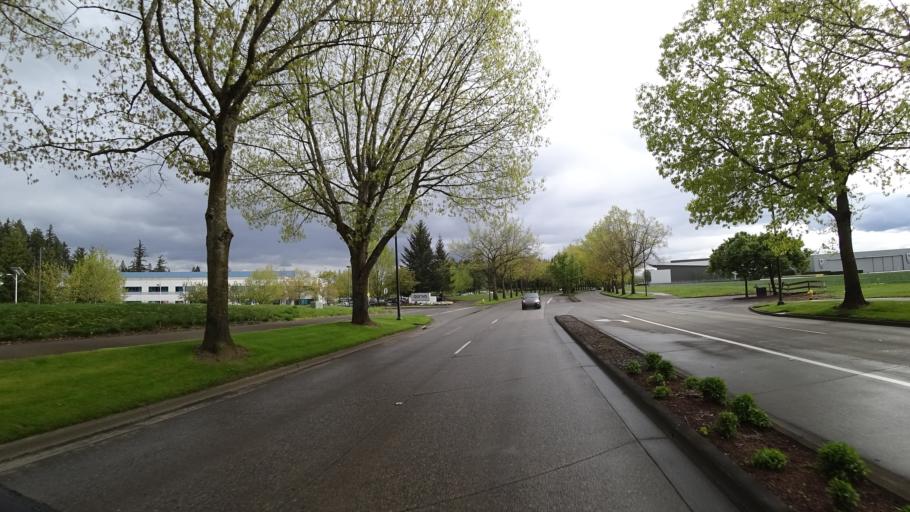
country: US
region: Oregon
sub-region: Washington County
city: Hillsboro
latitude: 45.5415
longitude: -122.9375
